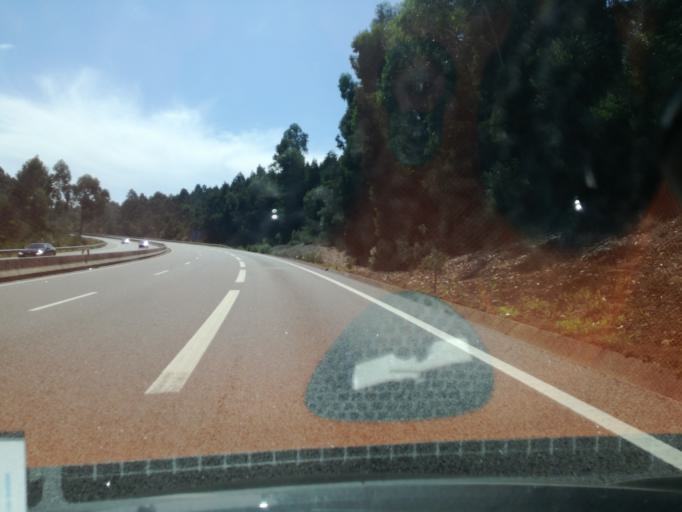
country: PT
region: Viana do Castelo
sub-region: Caminha
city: Vila Praia de Ancora
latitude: 41.7808
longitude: -8.7885
